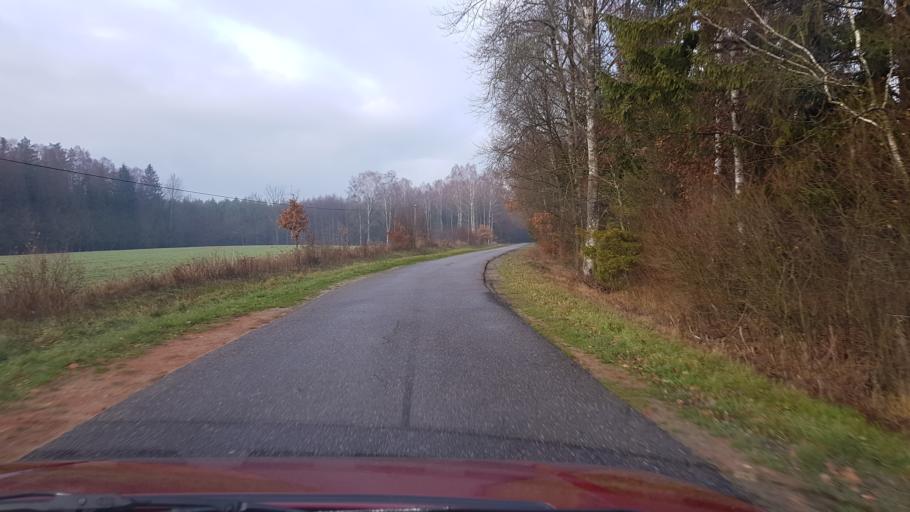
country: PL
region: West Pomeranian Voivodeship
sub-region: Powiat bialogardzki
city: Tychowo
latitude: 53.9476
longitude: 16.3147
